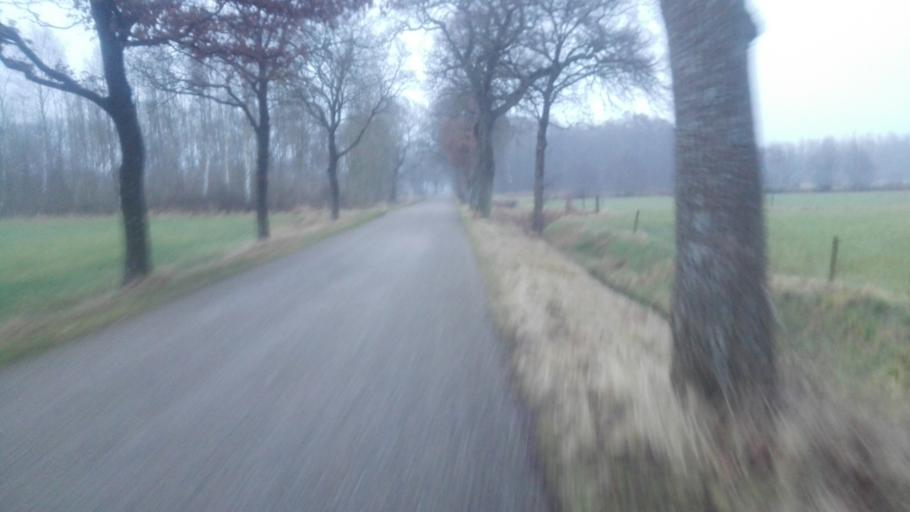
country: NL
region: Friesland
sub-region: Gemeente Heerenveen
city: Jubbega
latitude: 52.9551
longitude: 6.1629
